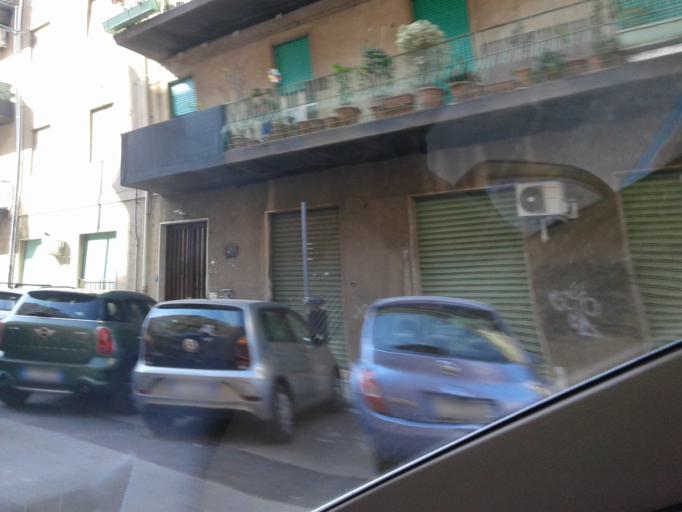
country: IT
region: Sicily
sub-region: Palermo
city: Palermo
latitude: 38.1308
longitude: 13.3432
